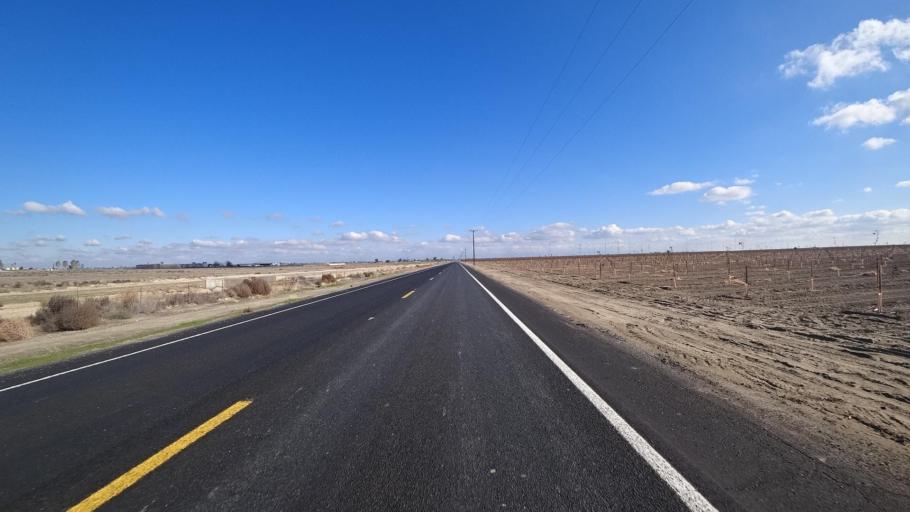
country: US
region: California
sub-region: Kern County
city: Delano
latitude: 35.7621
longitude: -119.3098
